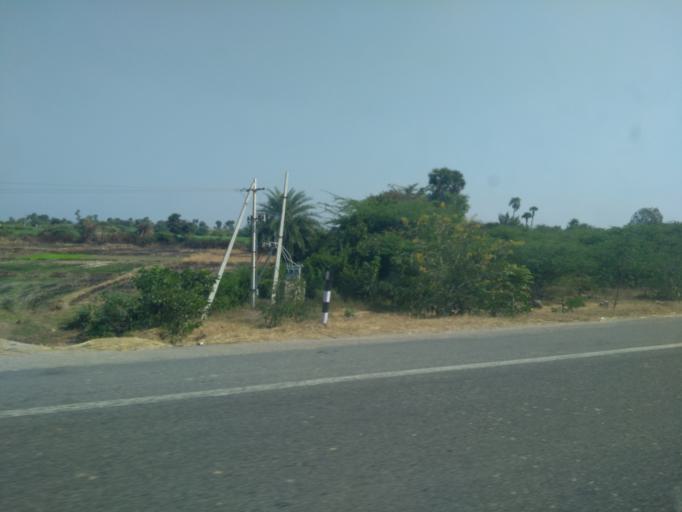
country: IN
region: Telangana
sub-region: Mahbubnagar
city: Wanparti
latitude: 16.4412
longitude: 77.9384
